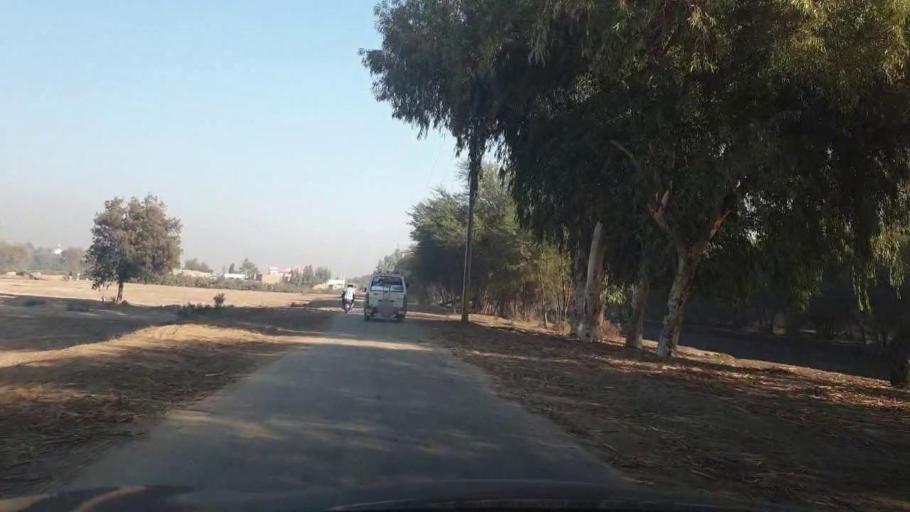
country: PK
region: Sindh
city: Mirpur Mathelo
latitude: 28.0704
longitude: 69.4668
